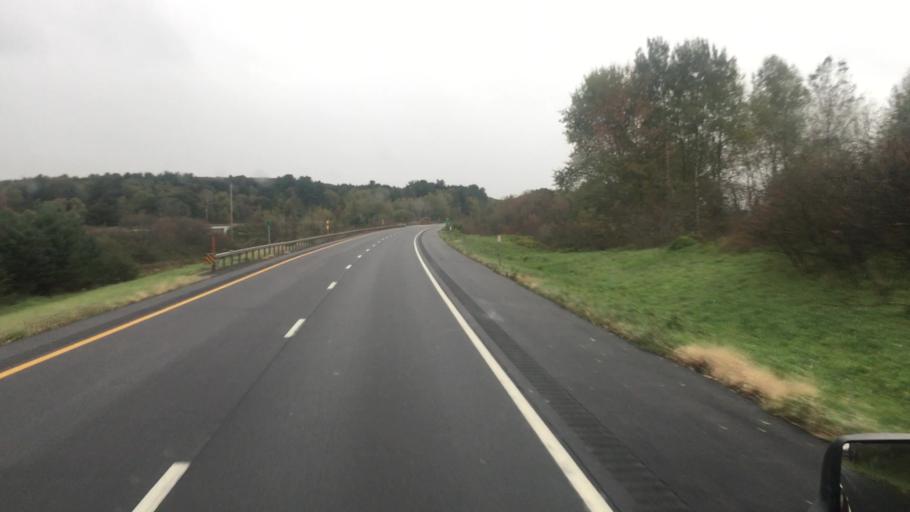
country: US
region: New York
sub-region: Chenango County
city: Bainbridge
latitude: 42.1983
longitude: -75.5402
